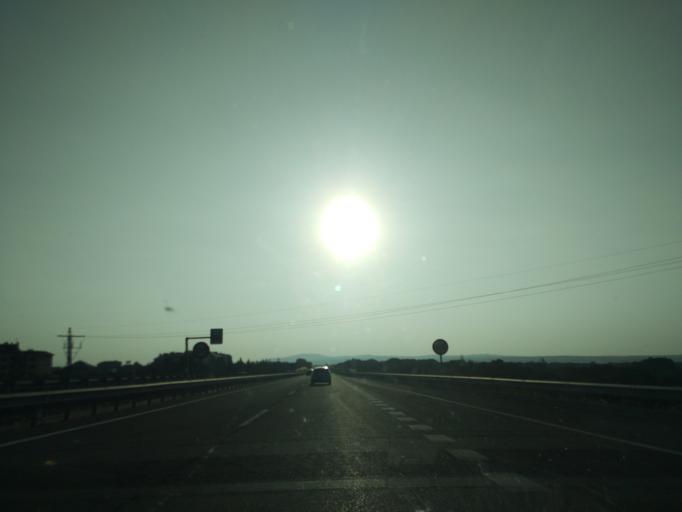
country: ES
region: Castille and Leon
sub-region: Provincia de Avila
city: Avila
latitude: 40.6710
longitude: -4.6564
